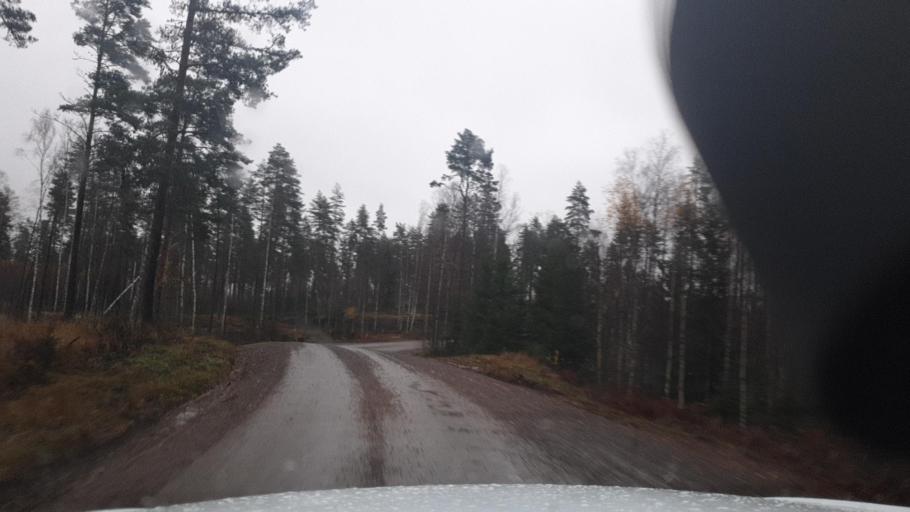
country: SE
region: Vaermland
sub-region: Eda Kommun
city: Charlottenberg
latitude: 59.7285
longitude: 12.1245
